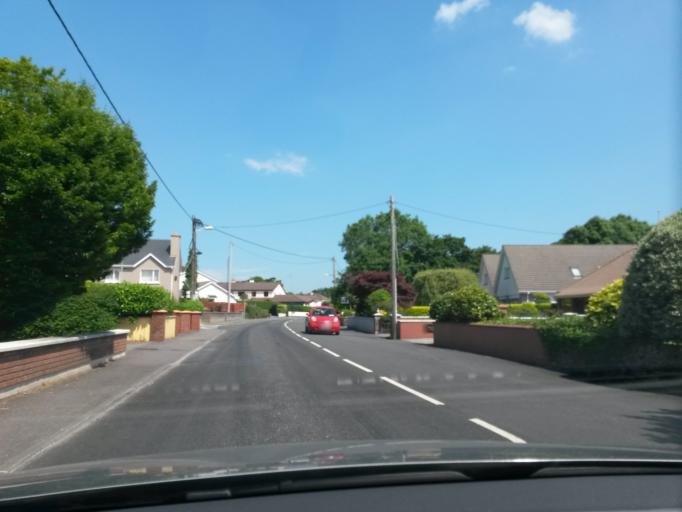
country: IE
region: Munster
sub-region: Ciarrai
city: Cill Airne
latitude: 52.0514
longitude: -9.5008
